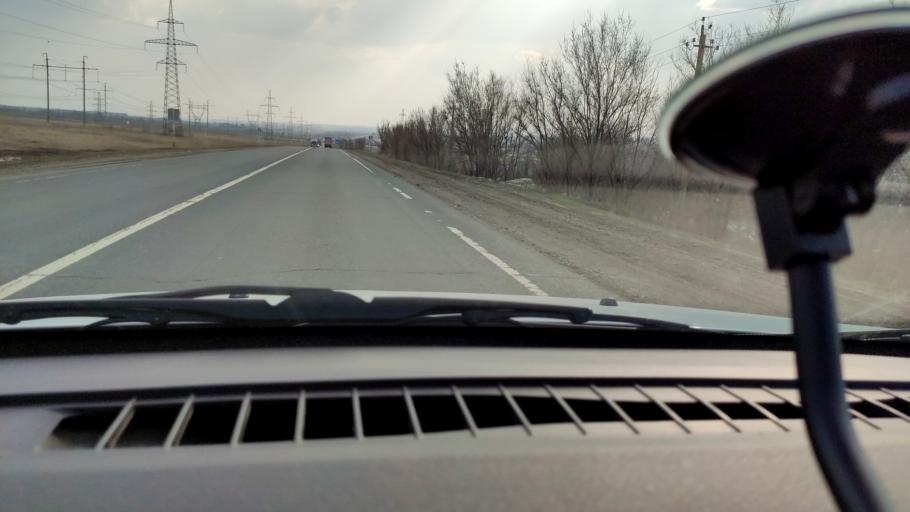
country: RU
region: Samara
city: Dubovyy Umet
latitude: 53.0697
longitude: 50.3817
